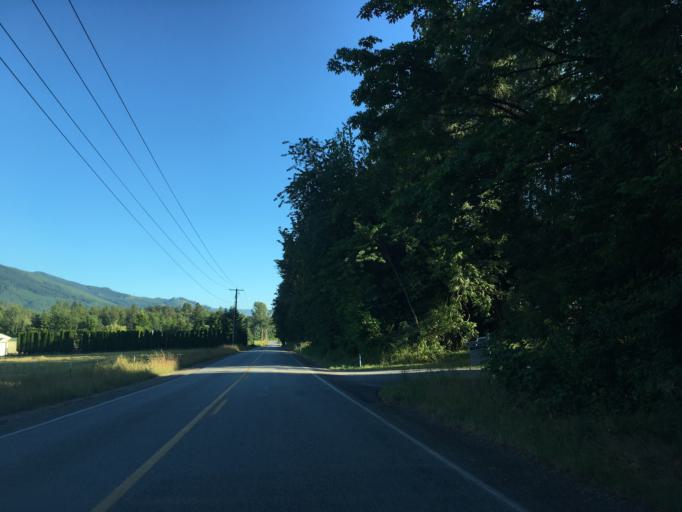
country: US
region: Washington
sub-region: Whatcom County
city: Nooksack
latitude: 48.9397
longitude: -122.2820
